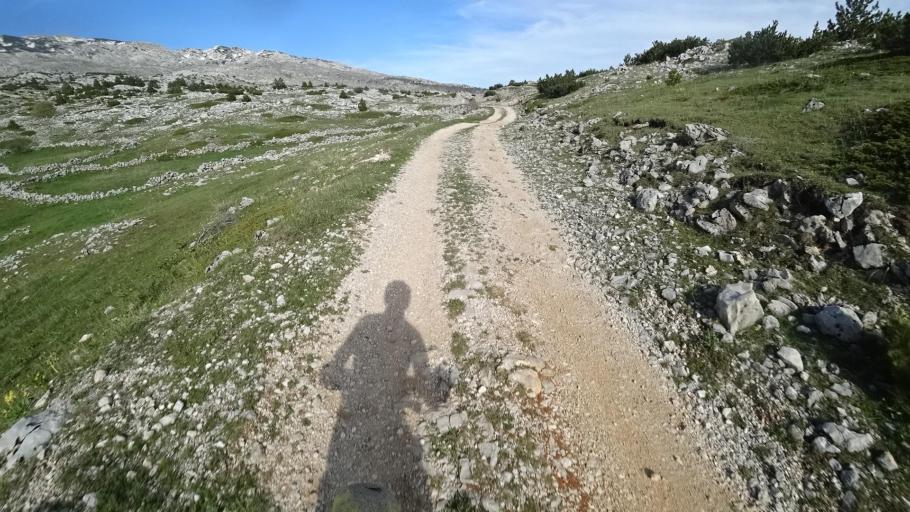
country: BA
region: Federation of Bosnia and Herzegovina
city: Kocerin
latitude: 43.5747
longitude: 17.5300
